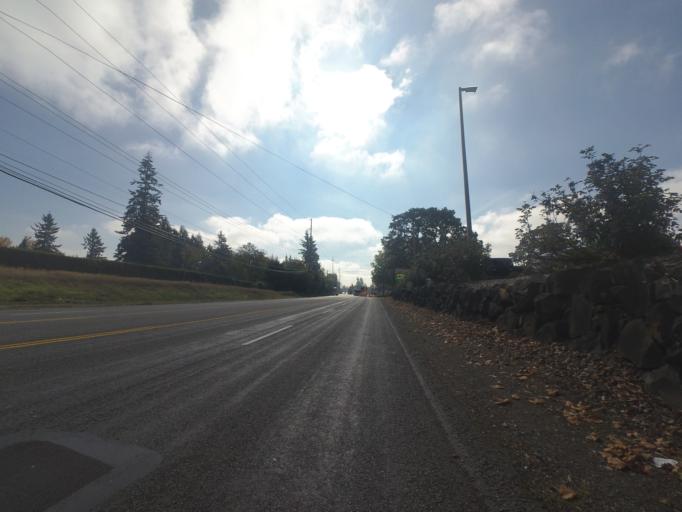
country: US
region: Washington
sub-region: Pierce County
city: Lakewood
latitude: 47.1927
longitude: -122.5088
